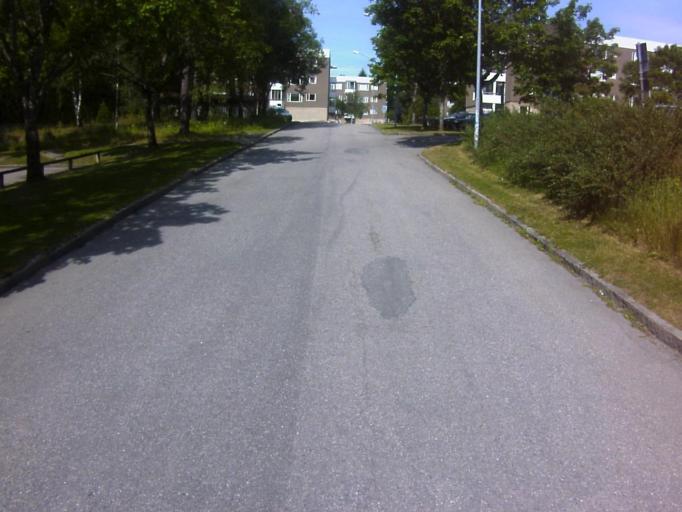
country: SE
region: Soedermanland
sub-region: Eskilstuna Kommun
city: Eskilstuna
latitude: 59.3542
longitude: 16.5328
